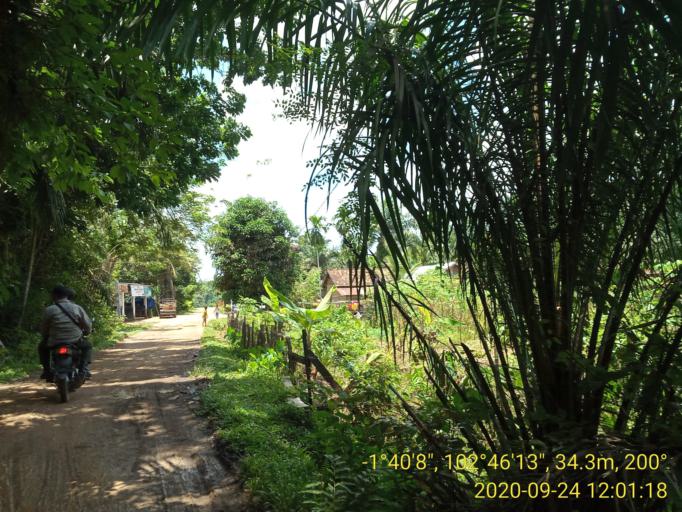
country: ID
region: Jambi
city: Sungaibengkal
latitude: -1.6689
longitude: 102.7705
